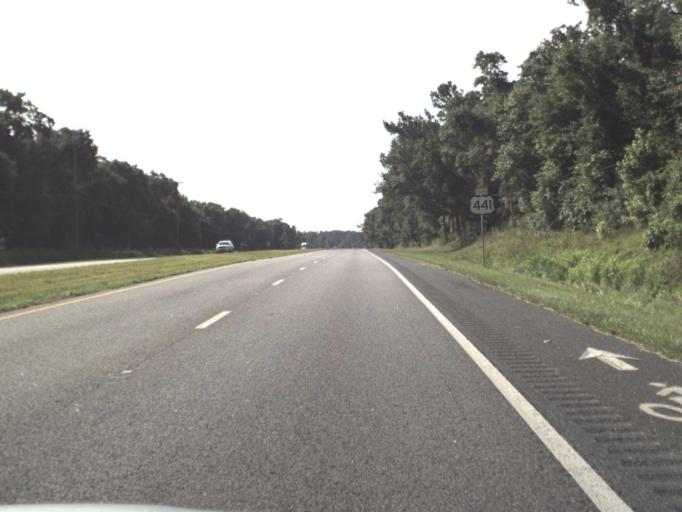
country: US
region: Florida
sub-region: Alachua County
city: Gainesville
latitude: 29.5219
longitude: -82.3025
